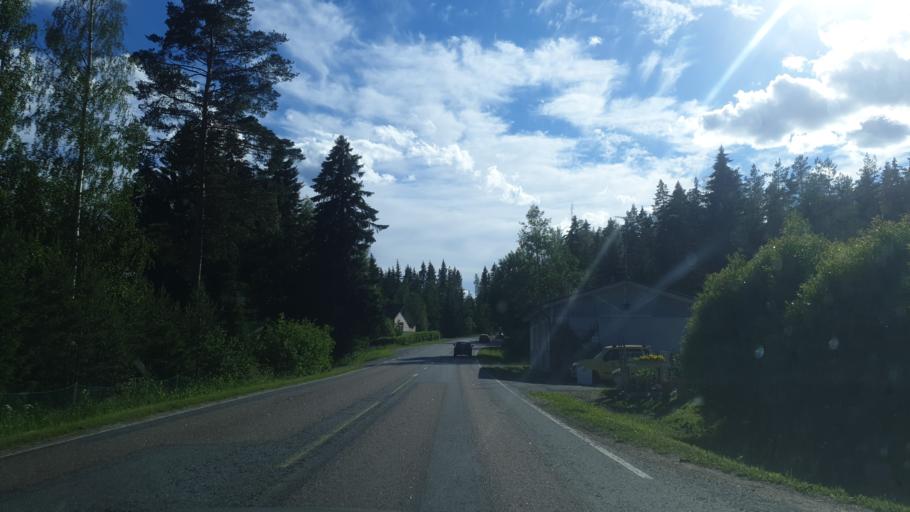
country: FI
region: Southern Savonia
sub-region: Mikkeli
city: Pertunmaa
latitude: 61.5202
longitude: 26.4987
